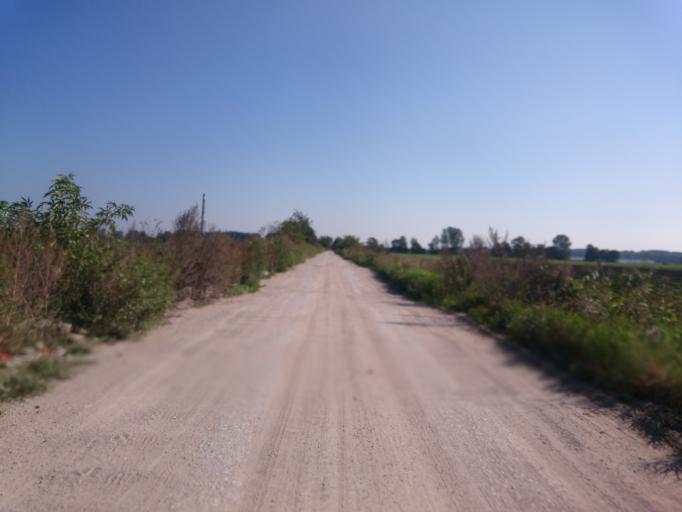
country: DE
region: Mecklenburg-Vorpommern
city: Barth
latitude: 54.3584
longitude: 12.6899
